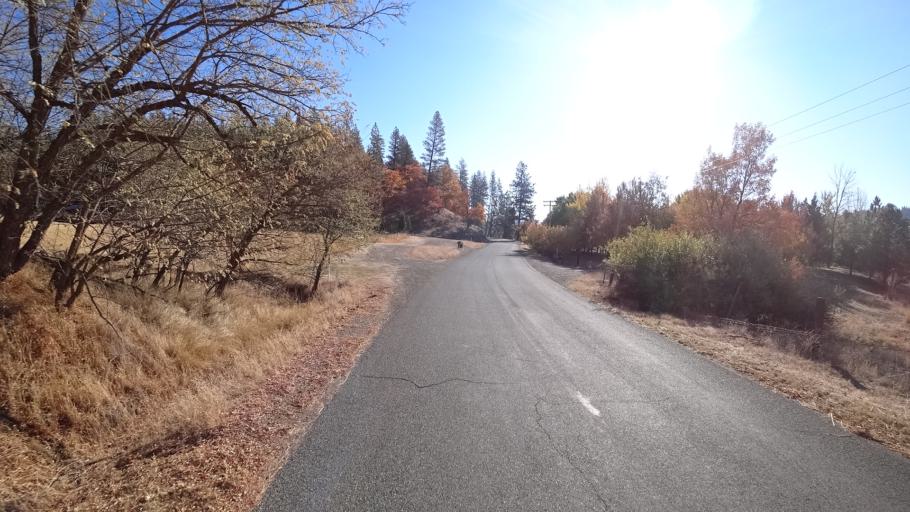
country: US
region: California
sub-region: Siskiyou County
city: Yreka
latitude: 41.6383
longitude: -122.9833
